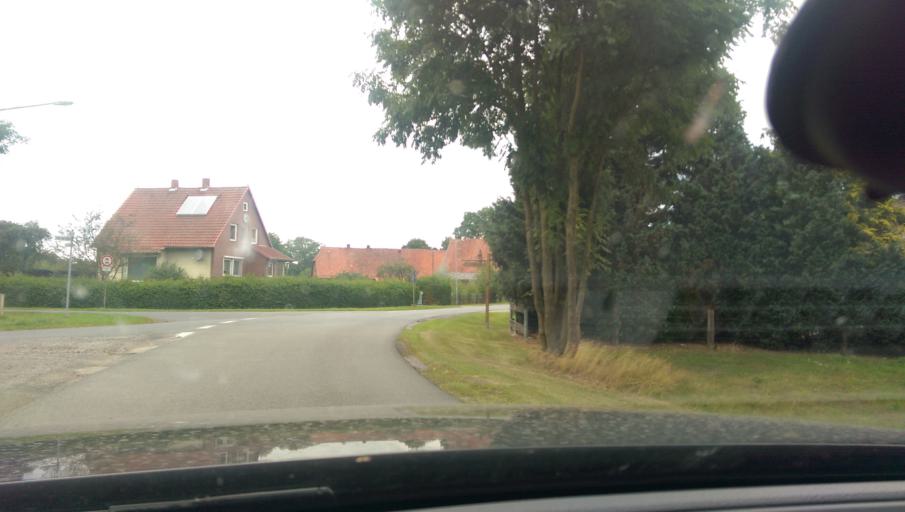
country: DE
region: Lower Saxony
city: Lindwedel
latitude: 52.6005
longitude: 9.6118
